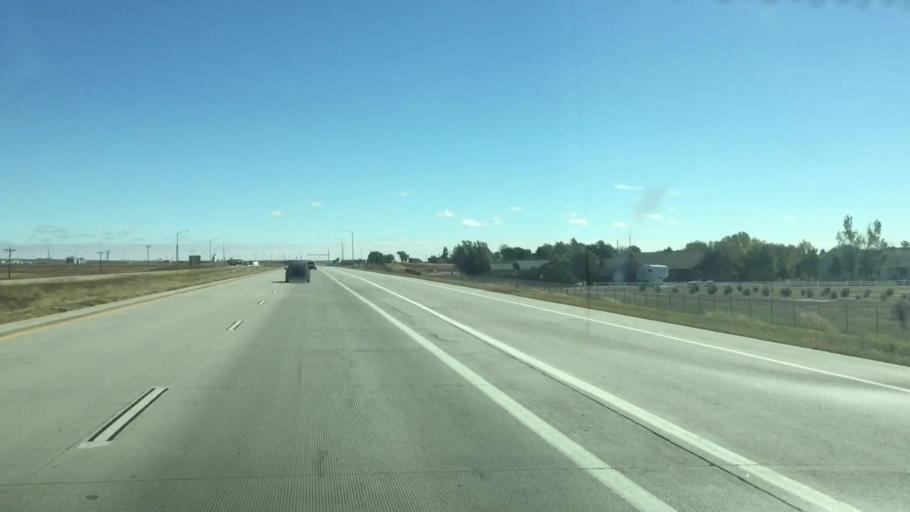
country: US
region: Colorado
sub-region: Lincoln County
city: Limon
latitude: 39.2732
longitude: -103.6936
